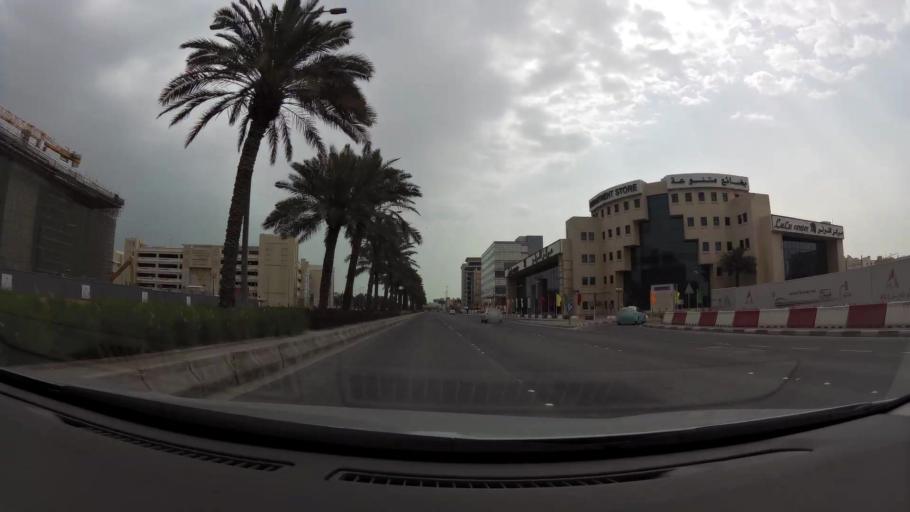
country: QA
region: Baladiyat ad Dawhah
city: Doha
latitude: 25.2914
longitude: 51.5016
